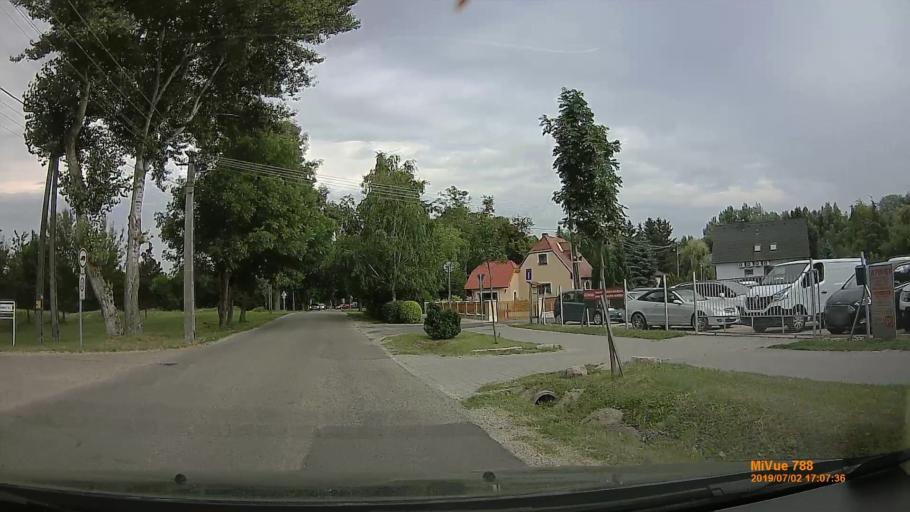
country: HU
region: Gyor-Moson-Sopron
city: Mosonmagyarovar
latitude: 47.8731
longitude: 17.2869
